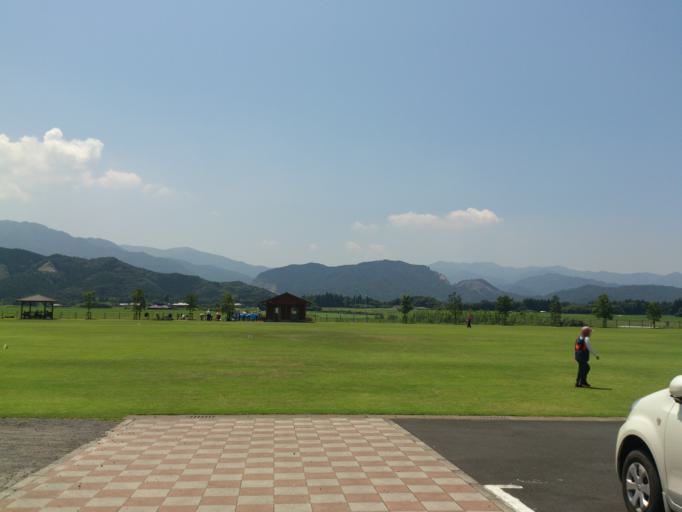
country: JP
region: Kagoshima
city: Kanoya
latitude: 31.3350
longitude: 130.9510
